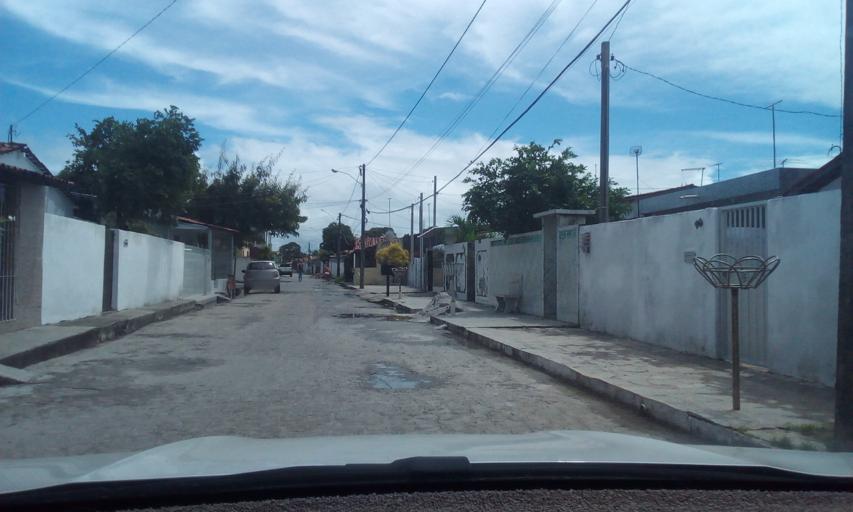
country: BR
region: Paraiba
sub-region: Cabedelo
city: Cabedelo
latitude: -6.9853
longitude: -34.8298
